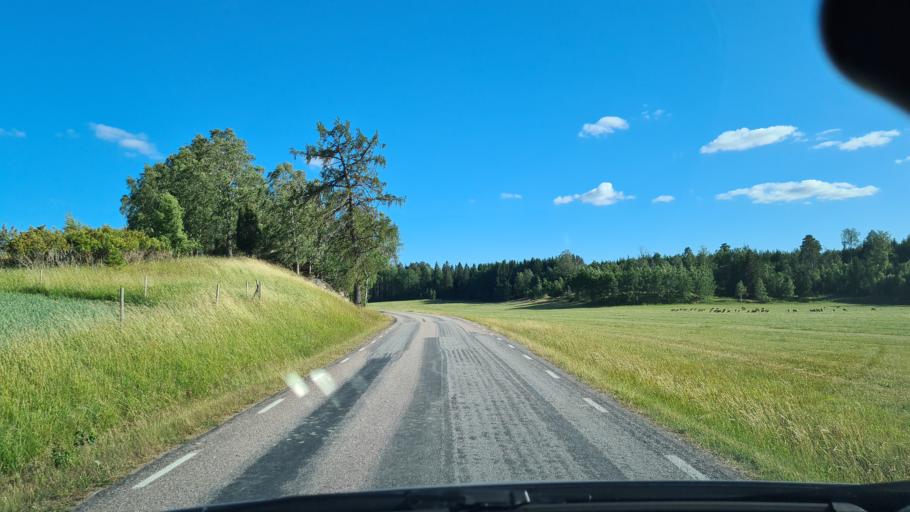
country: SE
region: Soedermanland
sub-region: Nykopings Kommun
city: Stigtomta
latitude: 58.9183
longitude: 16.8787
